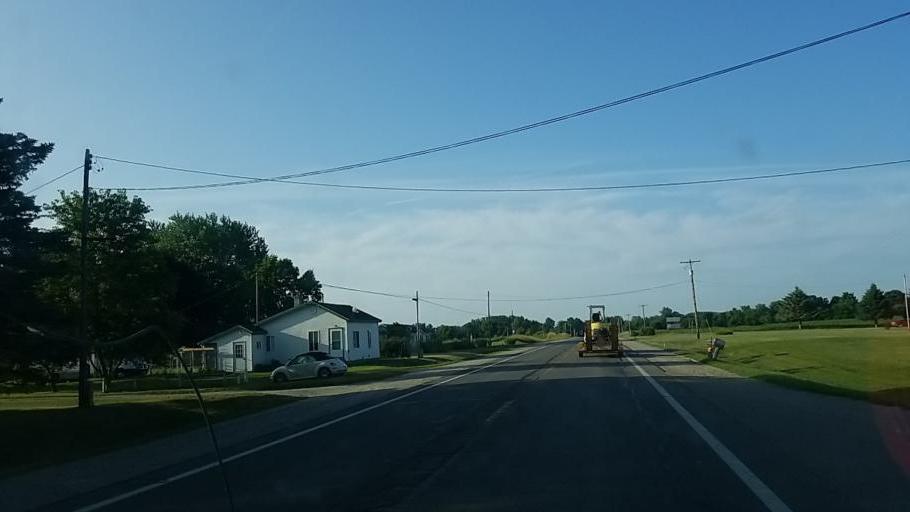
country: US
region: Michigan
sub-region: Montcalm County
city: Stanton
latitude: 43.1970
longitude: -85.0737
